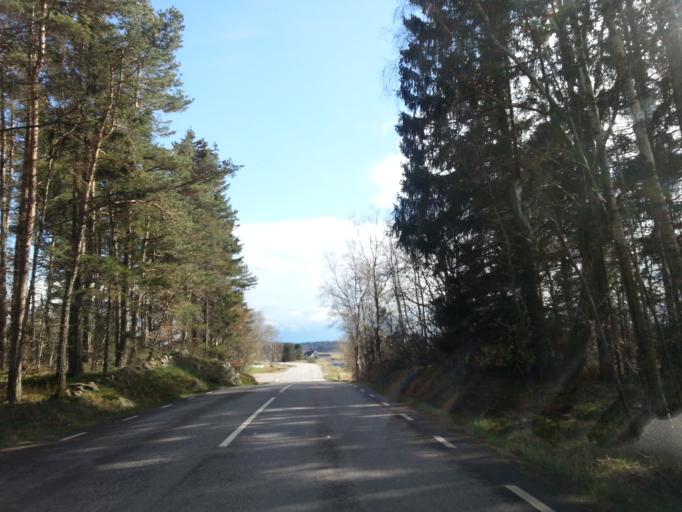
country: SE
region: Vaestra Goetaland
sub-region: Kungalvs Kommun
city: Kode
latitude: 57.9159
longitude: 11.9187
